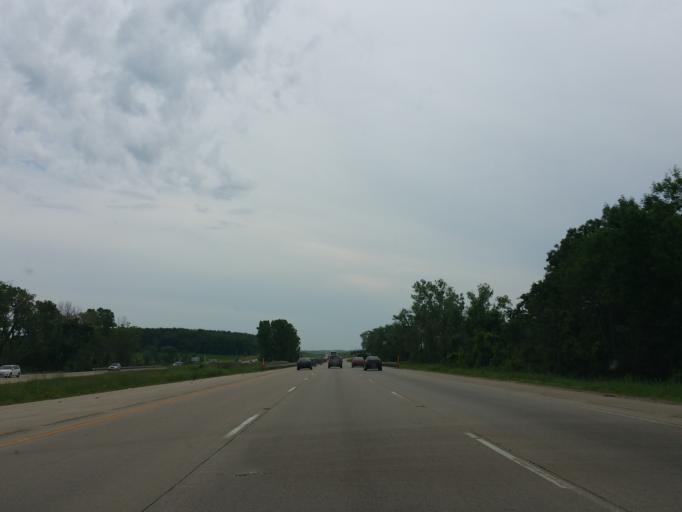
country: US
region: Wisconsin
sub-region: Columbia County
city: Poynette
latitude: 43.4388
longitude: -89.4873
